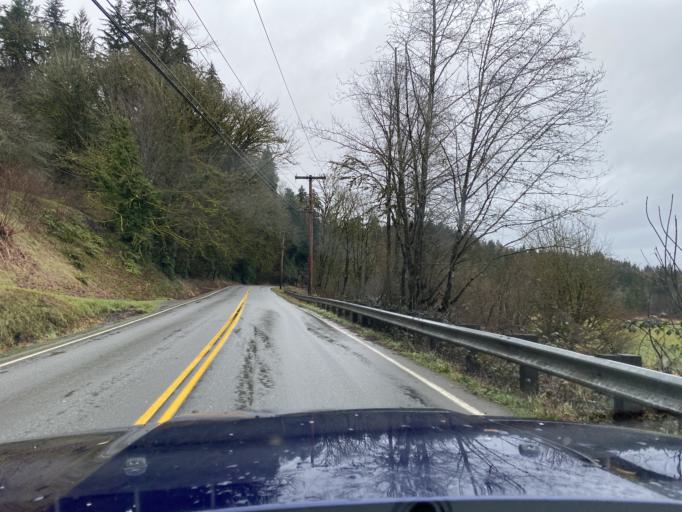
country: US
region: Washington
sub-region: King County
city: Duvall
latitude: 47.7329
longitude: -122.0127
